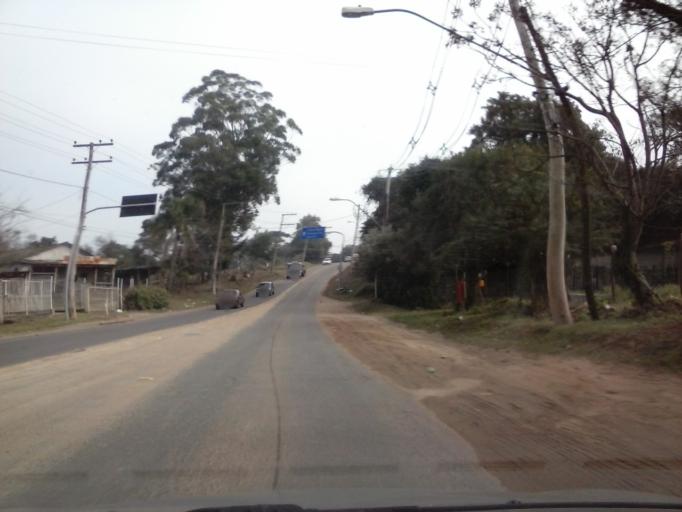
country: BR
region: Rio Grande do Sul
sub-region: Viamao
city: Viamao
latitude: -30.0463
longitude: -51.0859
